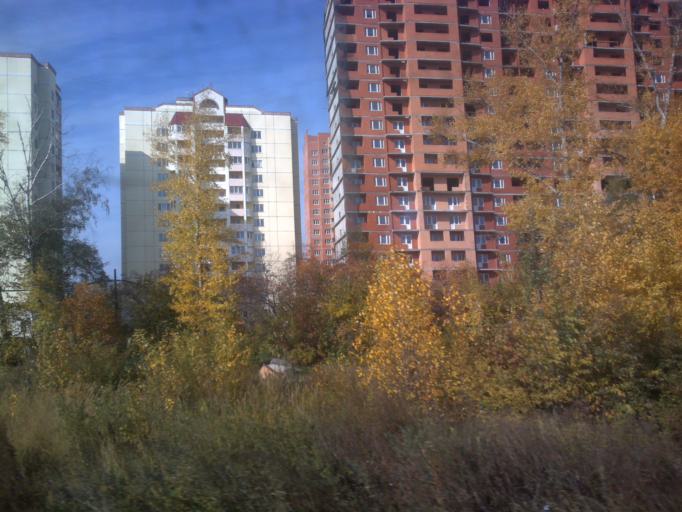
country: RU
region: Moskovskaya
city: Shcherbinka
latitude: 55.4924
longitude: 37.5568
